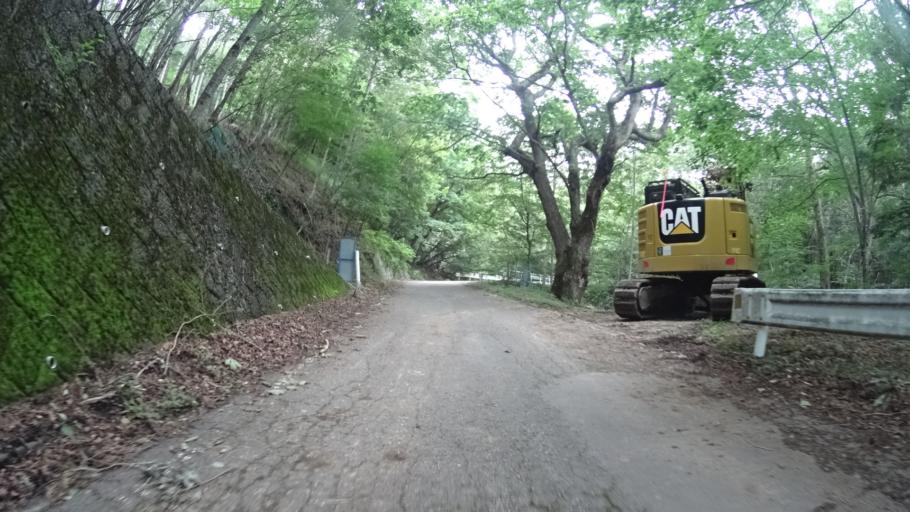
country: JP
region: Yamanashi
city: Kofu-shi
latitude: 35.8537
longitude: 138.5753
